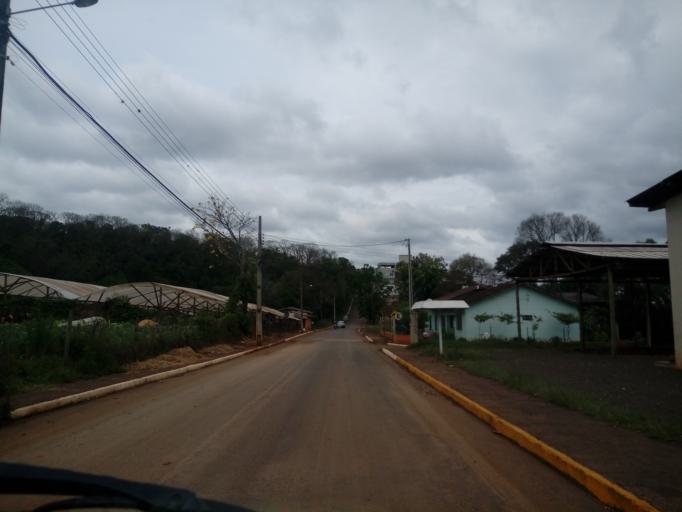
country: BR
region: Santa Catarina
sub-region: Chapeco
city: Chapeco
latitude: -27.0721
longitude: -52.6177
